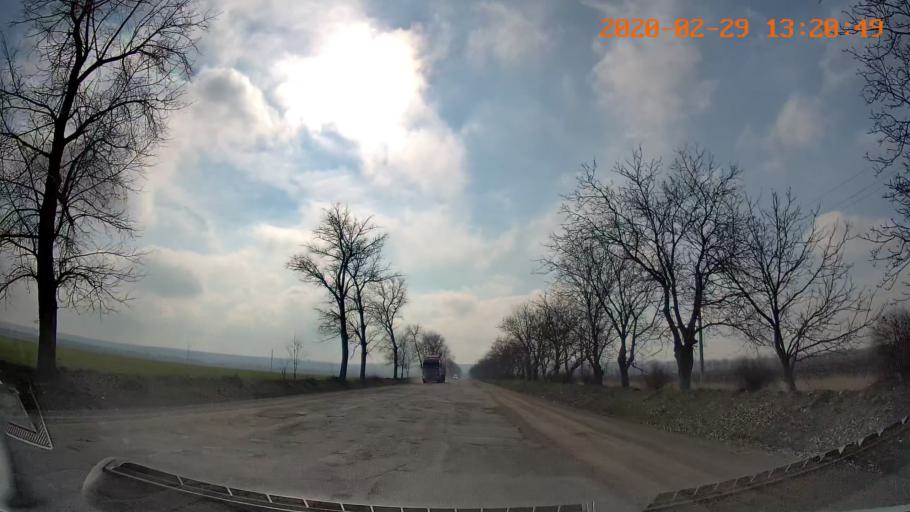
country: MD
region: Telenesti
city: Camenca
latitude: 47.9755
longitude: 28.6381
